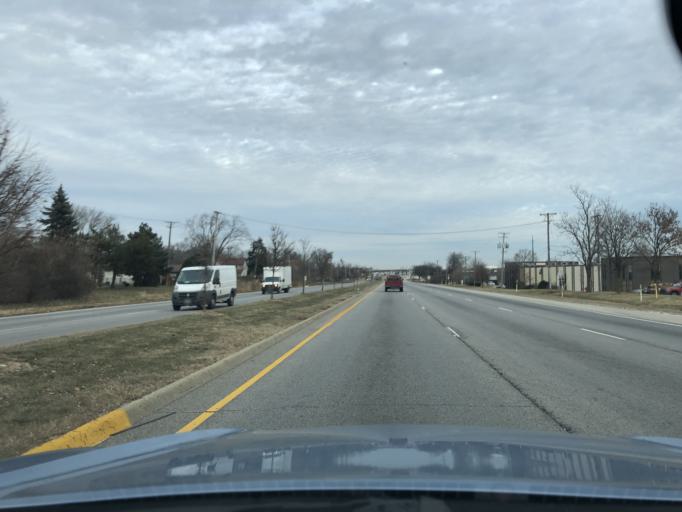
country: US
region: Illinois
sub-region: DuPage County
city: Wood Dale
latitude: 41.9746
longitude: -87.9592
